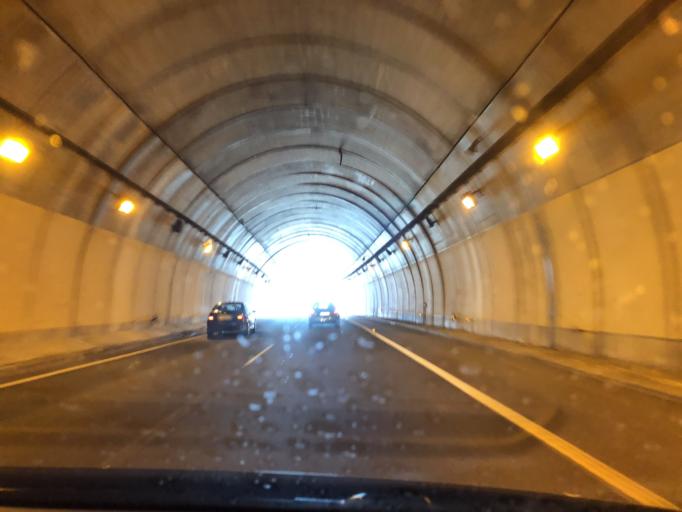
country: ES
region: Andalusia
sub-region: Provincia de Malaga
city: Manilva
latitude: 36.4242
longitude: -5.2122
